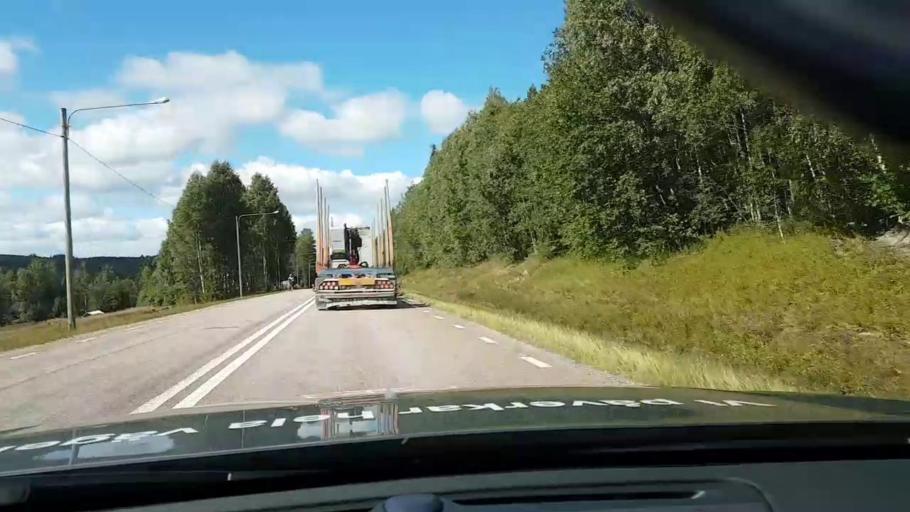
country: SE
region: Vaesternorrland
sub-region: OErnskoeldsviks Kommun
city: Bjasta
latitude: 63.3835
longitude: 18.3981
